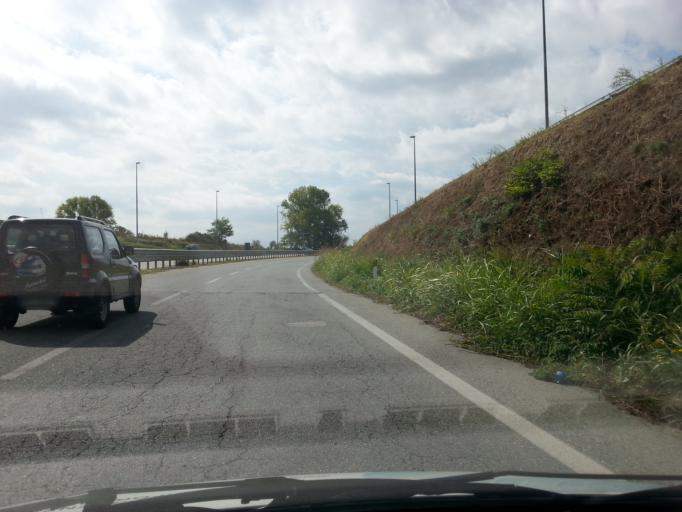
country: IT
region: Piedmont
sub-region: Provincia di Torino
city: Riva
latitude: 44.8879
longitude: 7.3580
